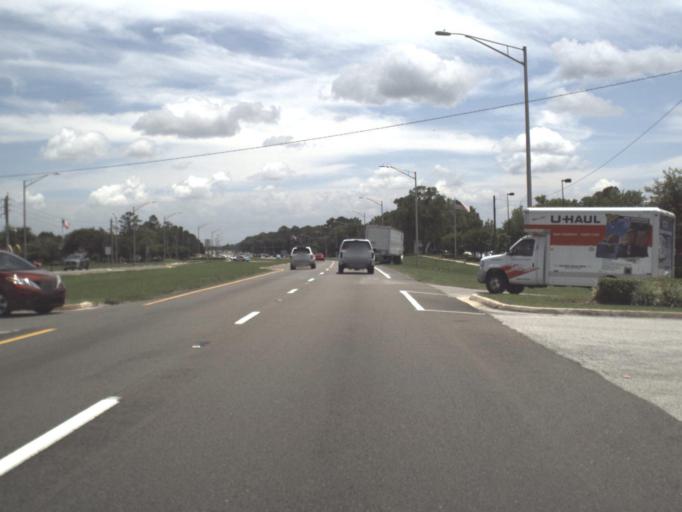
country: US
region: Florida
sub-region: Duval County
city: Jacksonville
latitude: 30.2664
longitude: -81.5585
